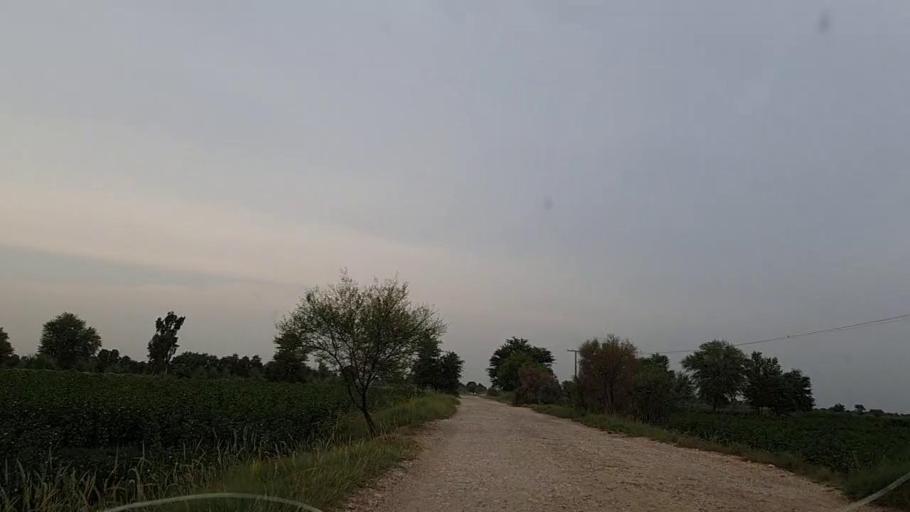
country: PK
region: Sindh
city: Mirpur Mathelo
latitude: 27.8639
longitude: 69.6324
